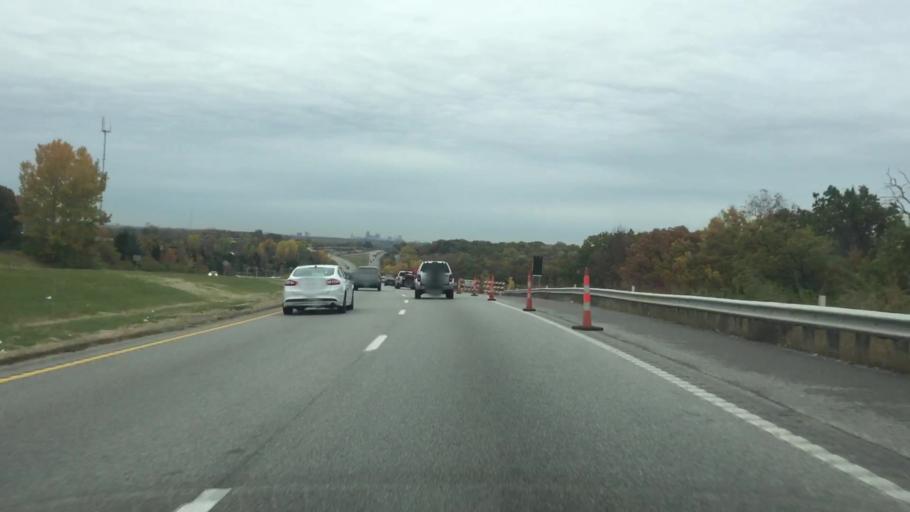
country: US
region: Missouri
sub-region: Jackson County
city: Raytown
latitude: 39.0068
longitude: -94.4861
